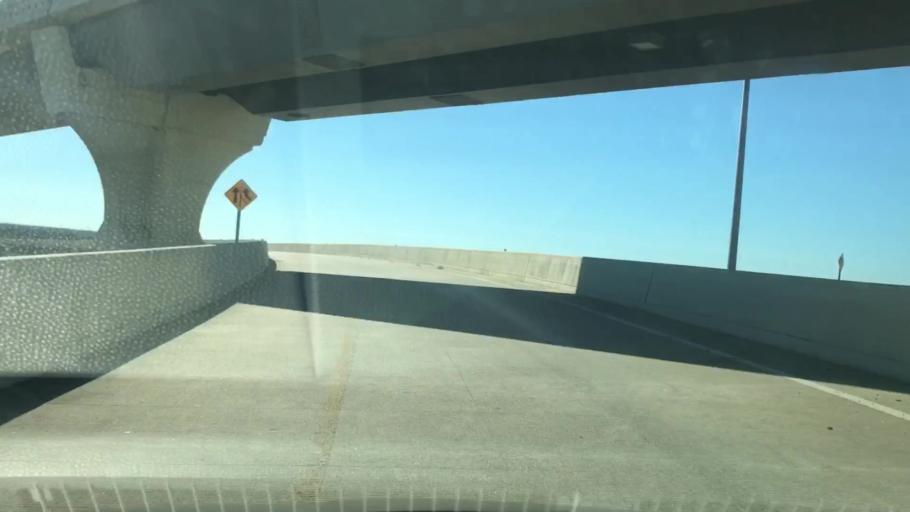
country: US
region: Texas
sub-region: Harris County
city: Cypress
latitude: 29.9974
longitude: -95.7685
